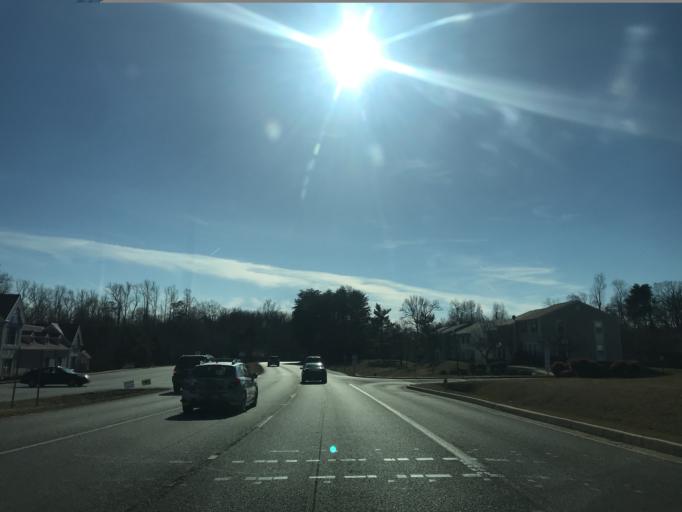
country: US
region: Maryland
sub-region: Charles County
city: Saint Charles
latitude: 38.6134
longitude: -76.8829
